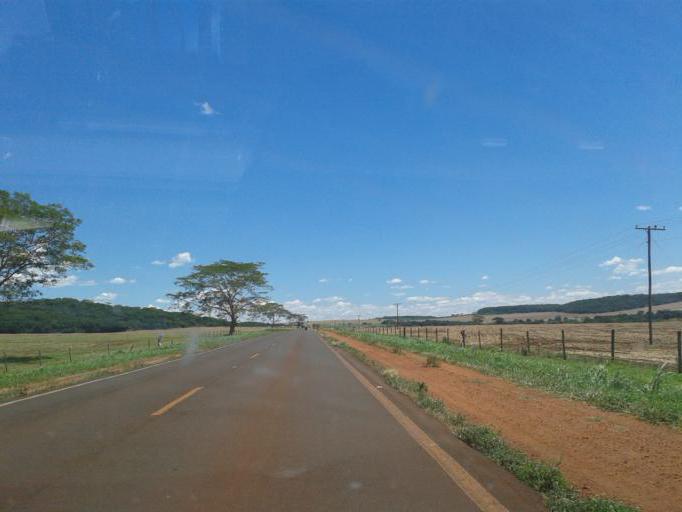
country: BR
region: Minas Gerais
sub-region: Capinopolis
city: Capinopolis
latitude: -18.6067
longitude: -49.5257
